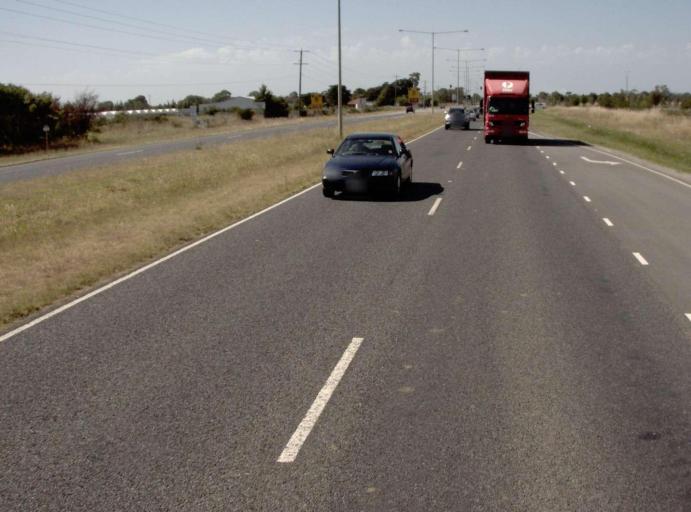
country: AU
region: Victoria
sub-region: Frankston
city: Sandhurst
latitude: -38.0509
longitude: 145.2083
